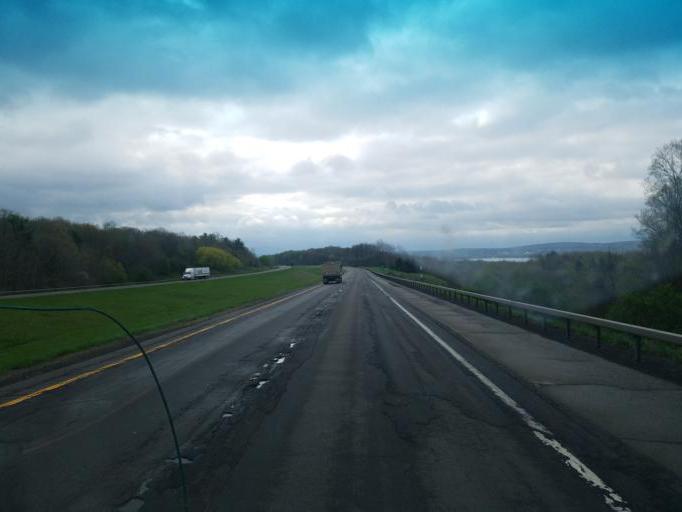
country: US
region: New York
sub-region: Chautauqua County
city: Lakewood
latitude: 42.1324
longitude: -79.3296
